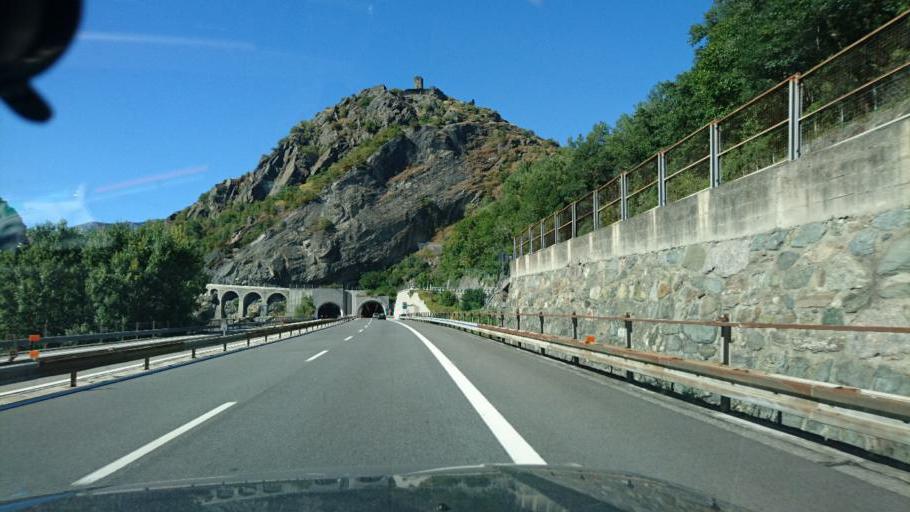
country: IT
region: Aosta Valley
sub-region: Valle d'Aosta
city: Montjovet
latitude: 45.7190
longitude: 7.6704
